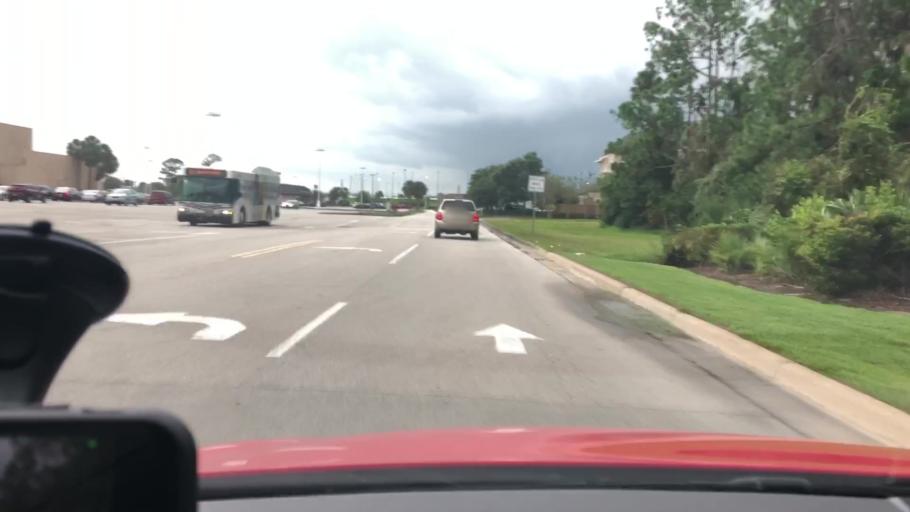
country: US
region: Florida
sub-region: Volusia County
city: Daytona Beach
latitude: 29.1967
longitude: -81.0671
